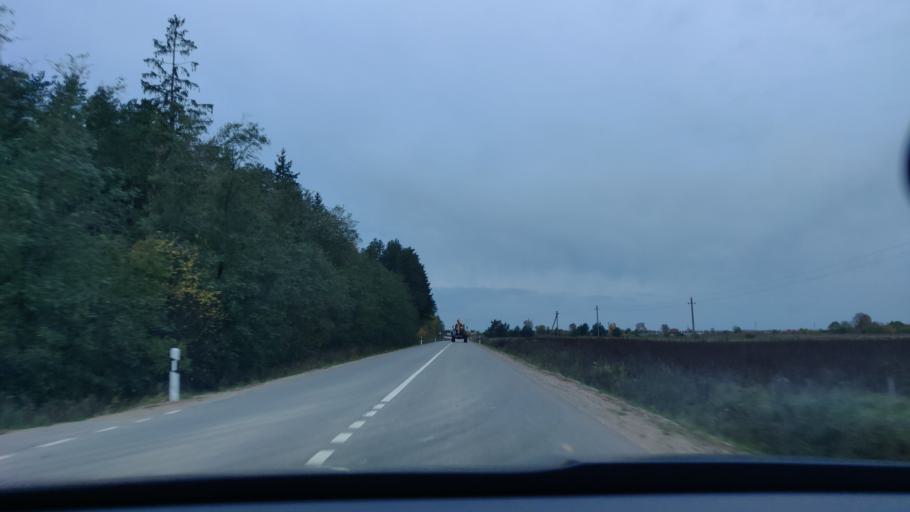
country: LT
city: Lentvaris
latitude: 54.5985
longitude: 25.0260
